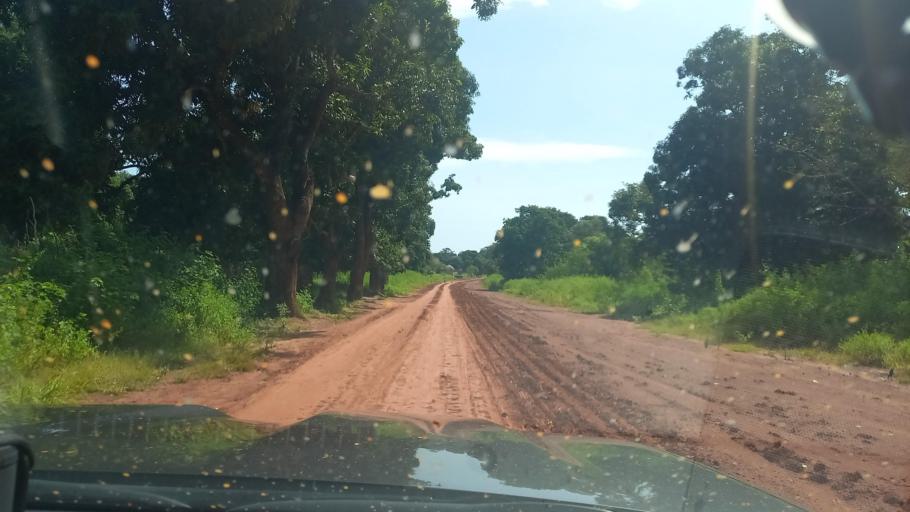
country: SN
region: Ziguinchor
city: Adeane
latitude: 12.6686
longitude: -16.0955
